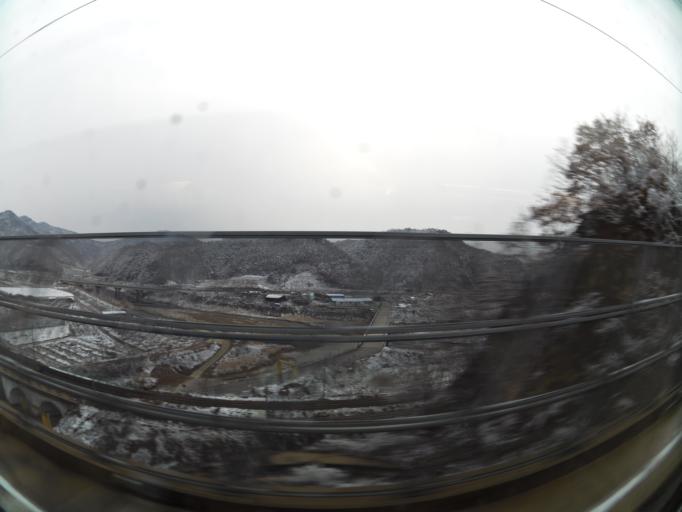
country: KR
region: Chungcheongbuk-do
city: Yong-dong
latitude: 36.2048
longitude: 127.7409
